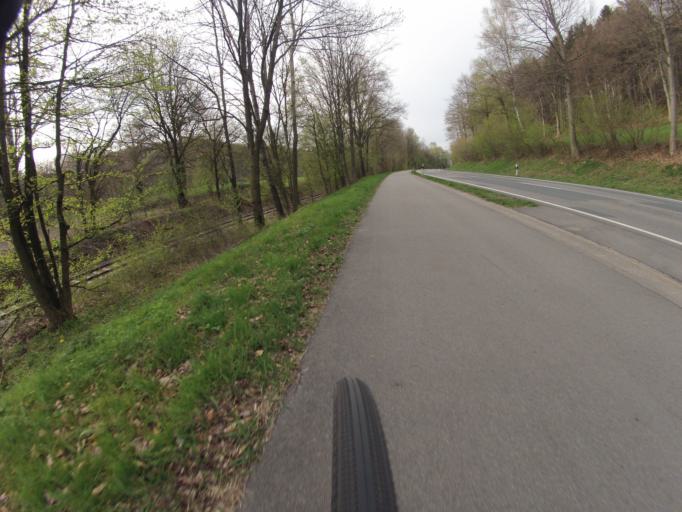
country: DE
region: North Rhine-Westphalia
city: Ibbenburen
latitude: 52.2363
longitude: 7.7419
